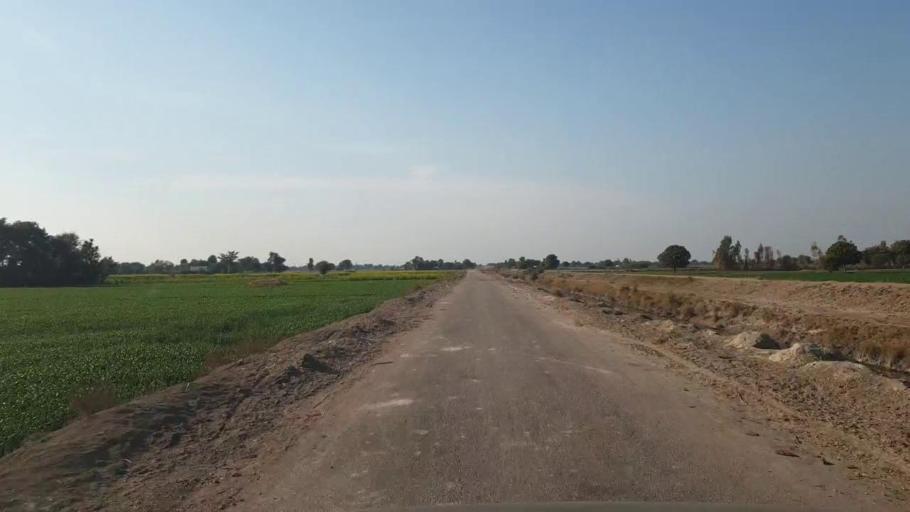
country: PK
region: Sindh
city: Shahpur Chakar
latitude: 26.1695
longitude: 68.6581
